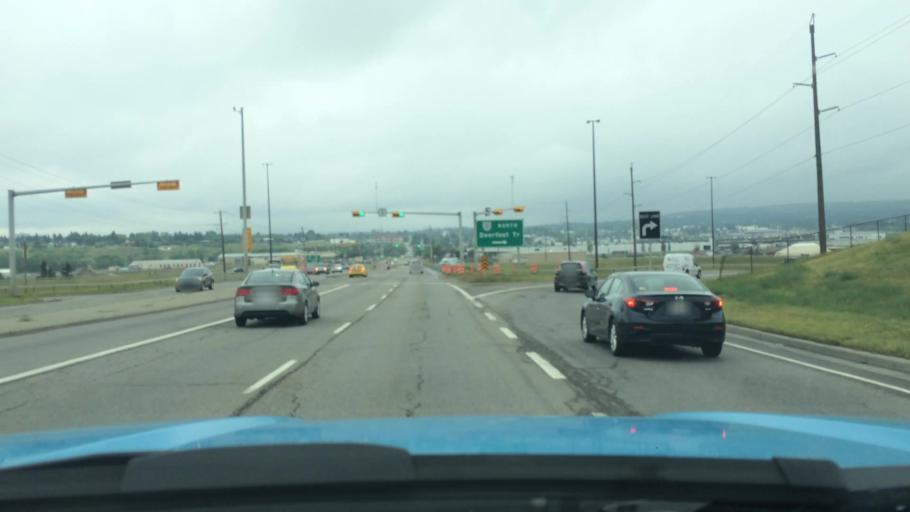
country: CA
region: Alberta
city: Calgary
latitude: 51.0816
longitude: -114.0319
